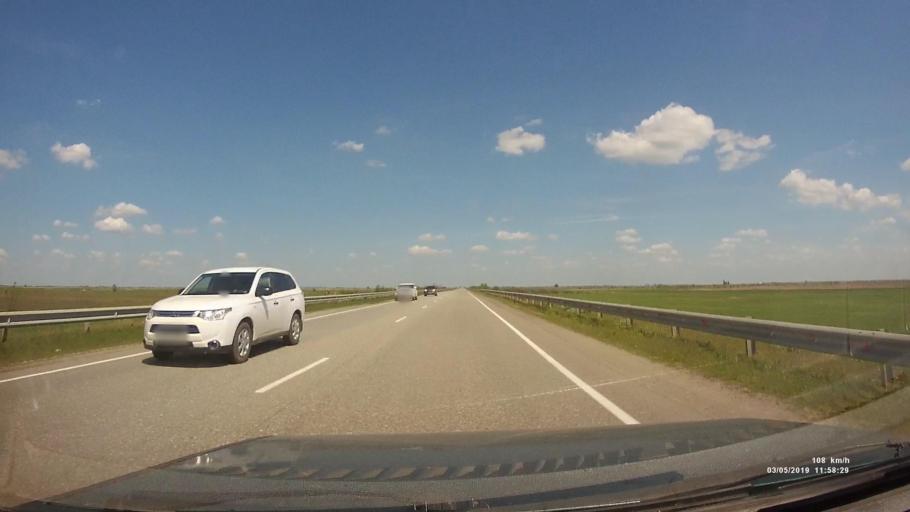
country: RU
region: Rostov
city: Bagayevskaya
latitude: 47.2215
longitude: 40.3207
